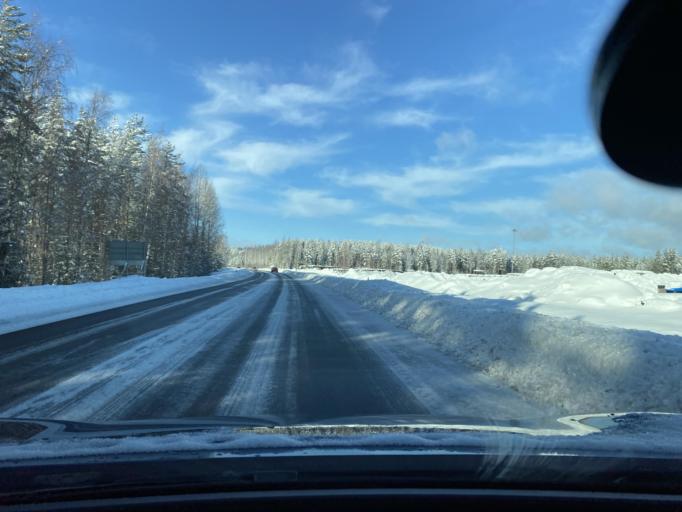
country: FI
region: Southern Savonia
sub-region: Mikkeli
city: Kangasniemi
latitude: 62.0091
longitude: 26.6390
